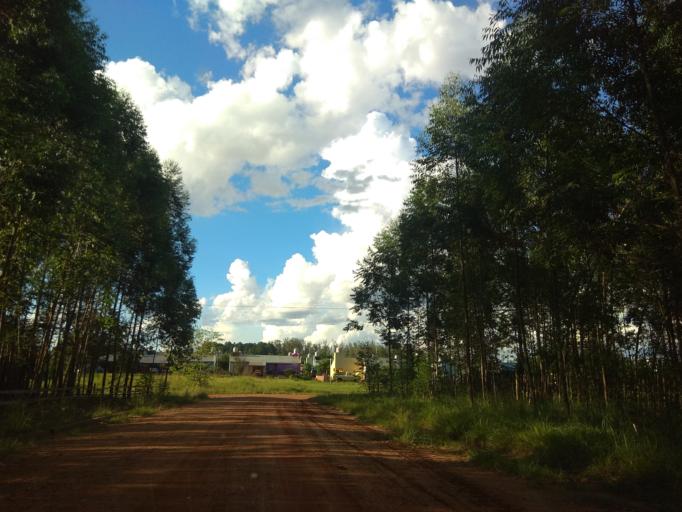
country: AR
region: Misiones
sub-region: Departamento de Candelaria
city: Candelaria
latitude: -27.4803
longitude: -55.7515
